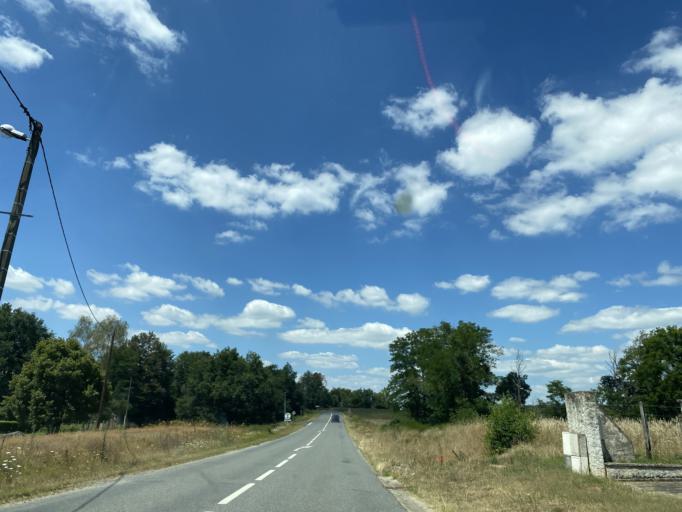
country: FR
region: Auvergne
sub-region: Departement du Puy-de-Dome
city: Peschadoires
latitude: 45.8688
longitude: 3.4904
